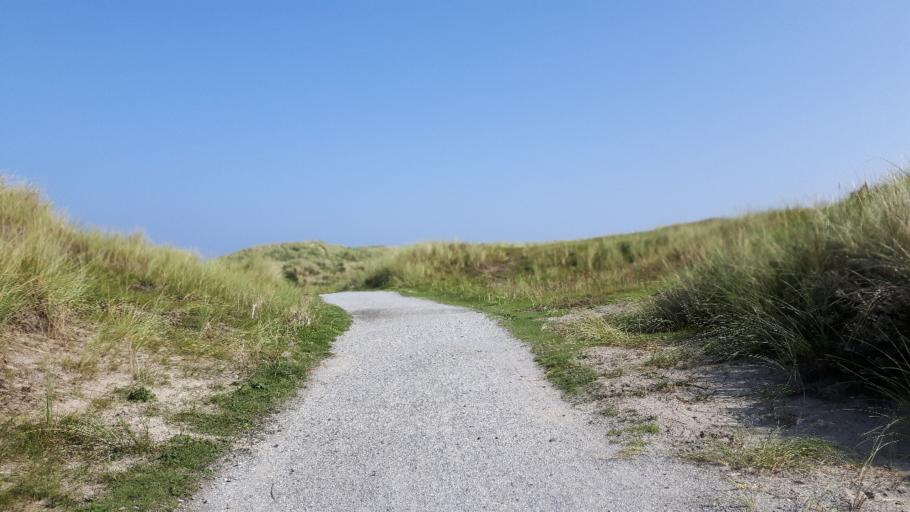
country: NL
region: Friesland
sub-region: Gemeente Ameland
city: Nes
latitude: 53.4603
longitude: 5.8167
